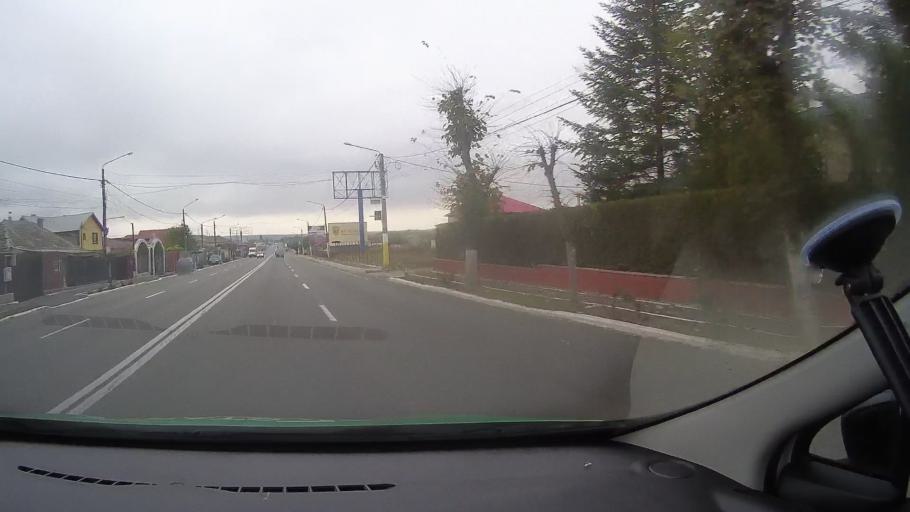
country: RO
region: Constanta
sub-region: Comuna Valu lui Traian
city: Valu lui Traian
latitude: 44.1682
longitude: 28.4488
